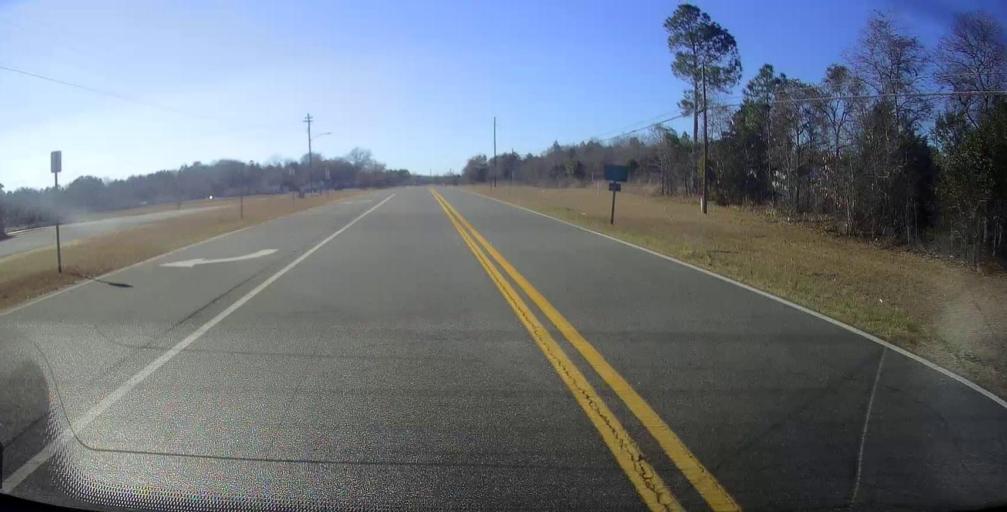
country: US
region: Georgia
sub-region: Taylor County
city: Butler
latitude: 32.5559
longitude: -84.2205
